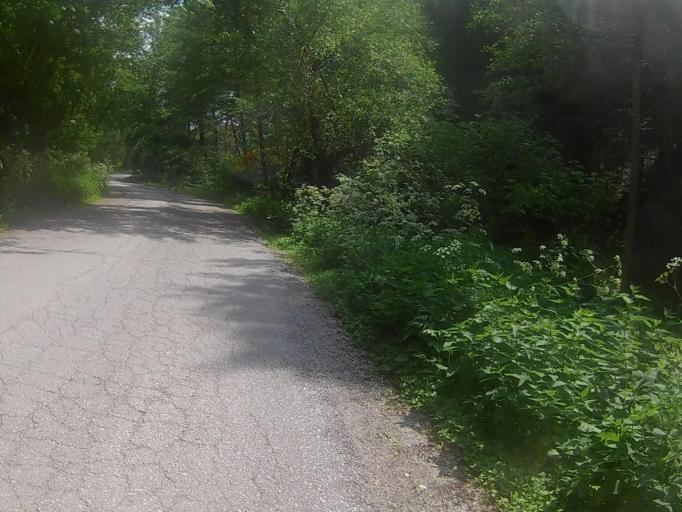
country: SI
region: Kungota
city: Zgornja Kungota
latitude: 46.6181
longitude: 15.5807
